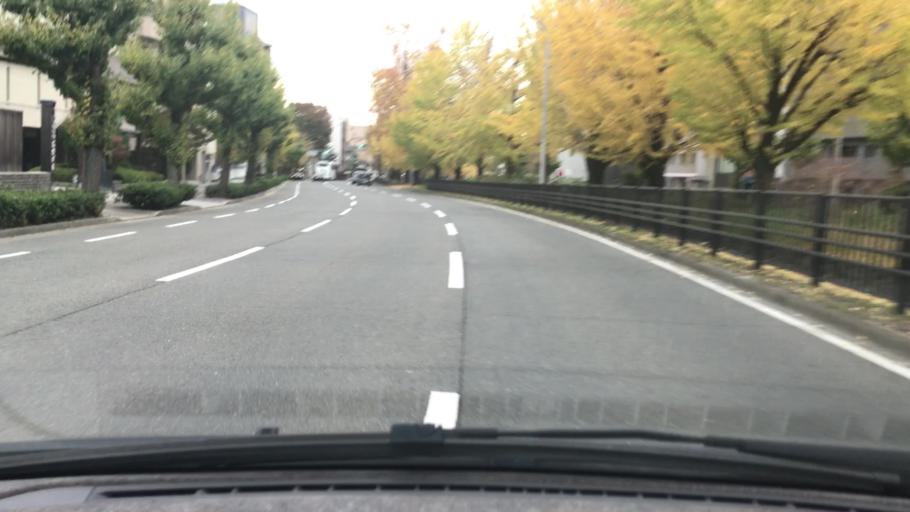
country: JP
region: Kyoto
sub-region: Kyoto-shi
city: Kamigyo-ku
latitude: 35.0351
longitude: 135.7514
